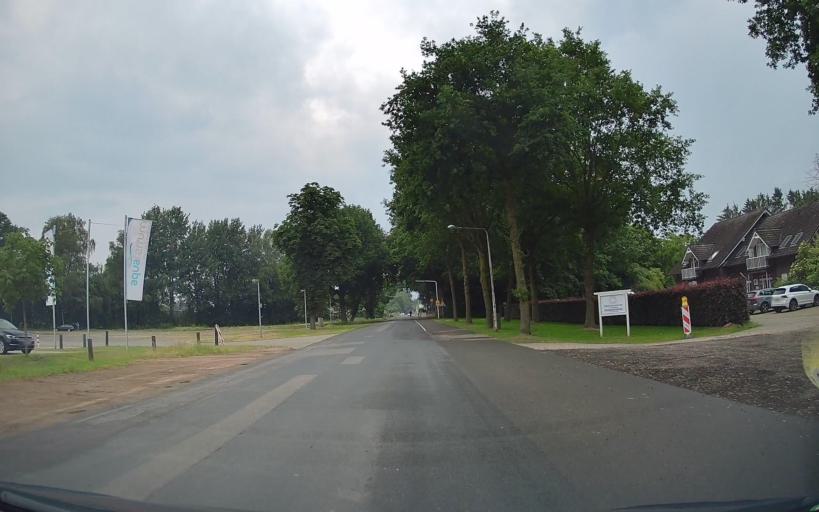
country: DE
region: Lower Saxony
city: Friesoythe
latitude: 53.0121
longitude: 7.8614
